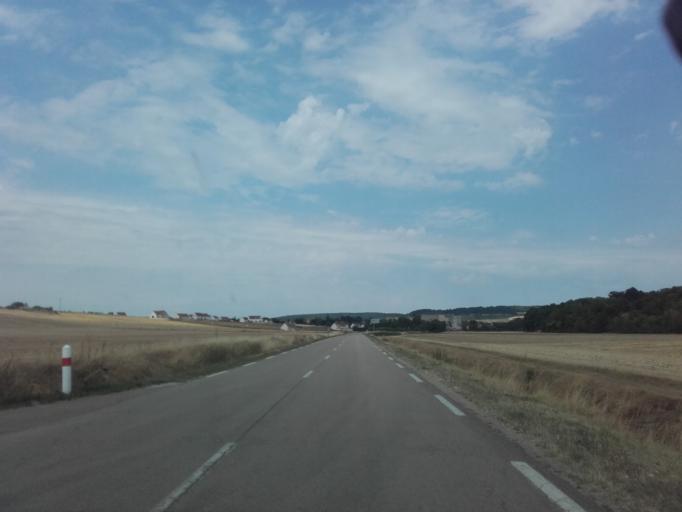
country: FR
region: Bourgogne
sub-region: Departement de l'Yonne
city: Chablis
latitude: 47.7998
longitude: 3.7985
